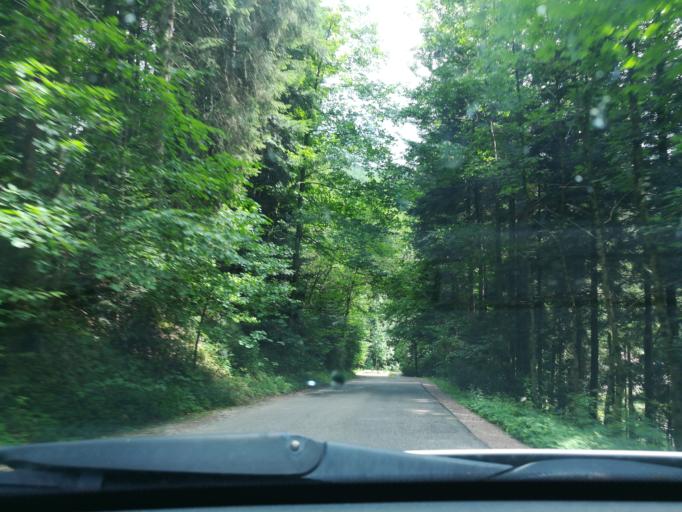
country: DE
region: Baden-Wuerttemberg
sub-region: Freiburg Region
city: Aichhalden
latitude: 48.2621
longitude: 8.3982
